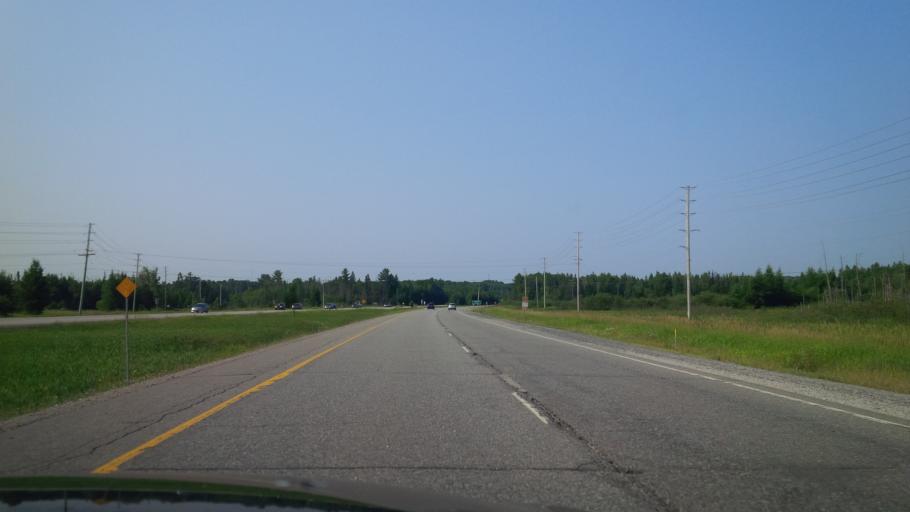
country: CA
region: Ontario
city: Huntsville
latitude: 45.2395
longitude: -79.3007
